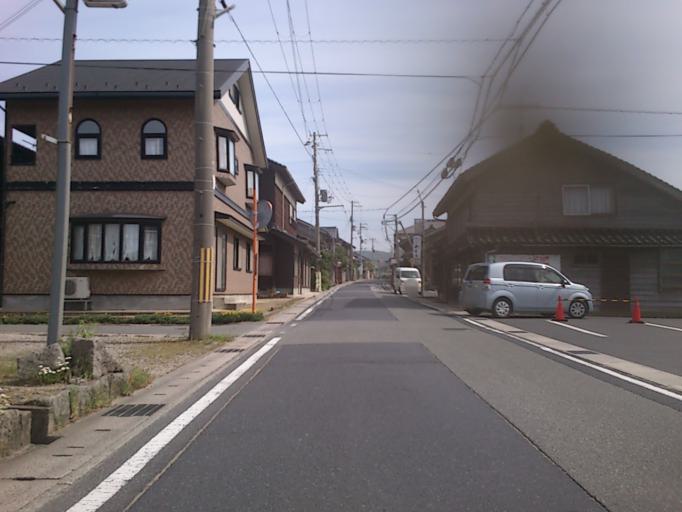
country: JP
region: Hyogo
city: Toyooka
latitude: 35.6644
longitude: 134.9682
